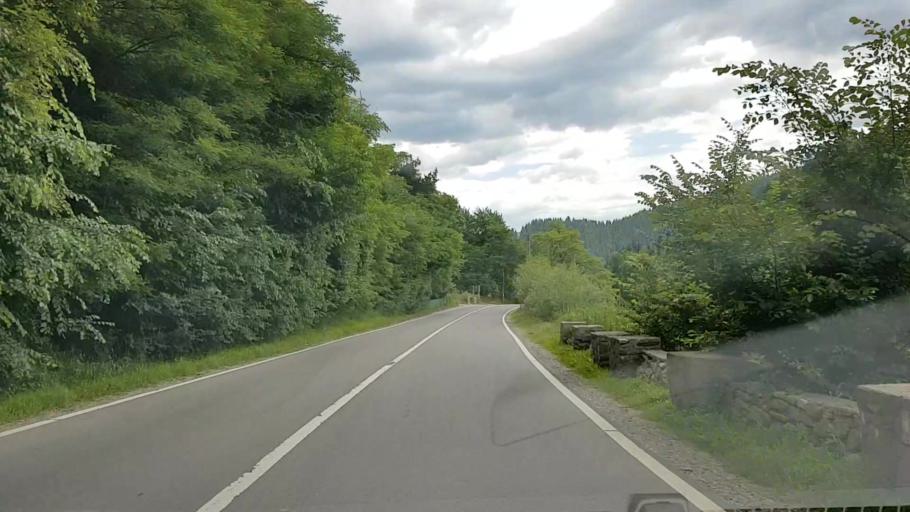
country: RO
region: Neamt
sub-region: Comuna Farcasa
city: Farcasa
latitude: 47.1591
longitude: 25.8299
